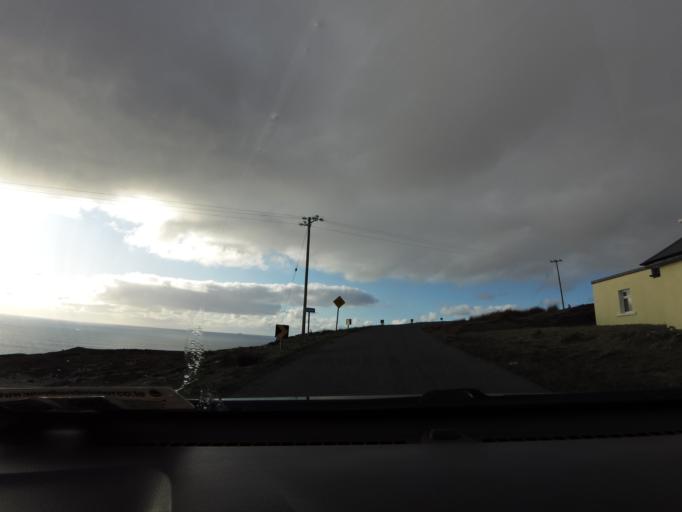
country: IE
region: Connaught
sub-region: Maigh Eo
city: Belmullet
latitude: 53.9066
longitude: -9.9944
